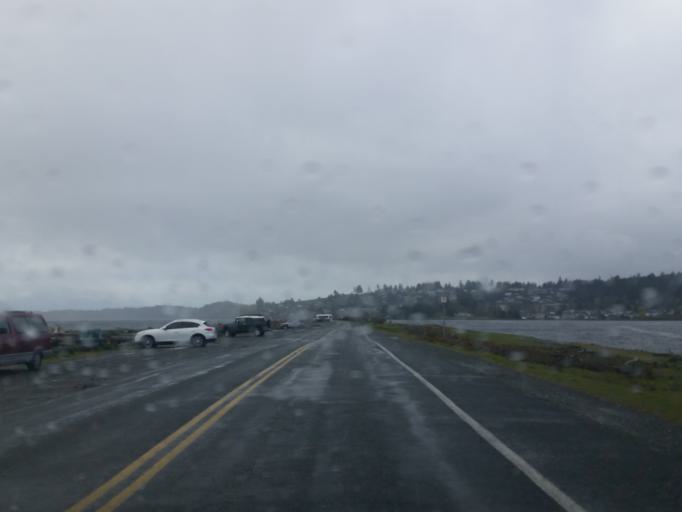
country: CA
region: British Columbia
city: Colwood
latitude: 48.4289
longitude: -123.4591
